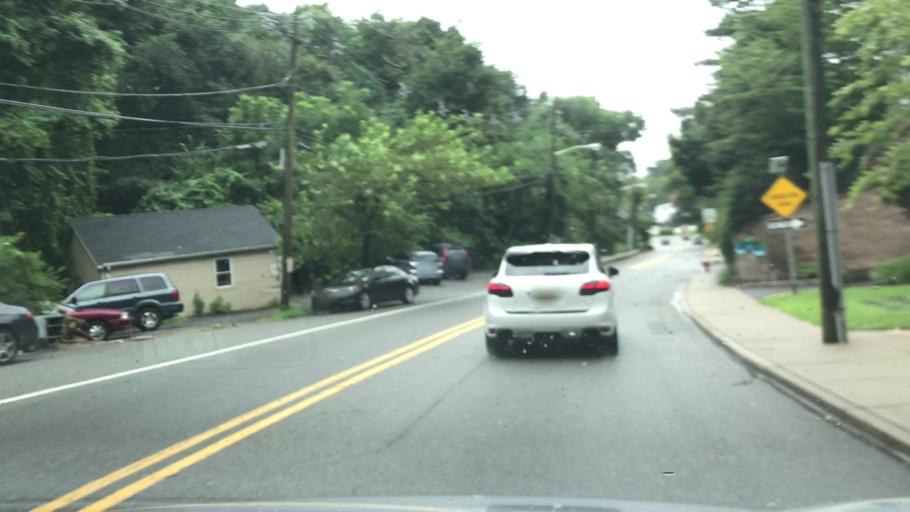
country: US
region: New Jersey
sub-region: Bergen County
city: Fort Lee
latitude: 40.8465
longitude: -73.9664
